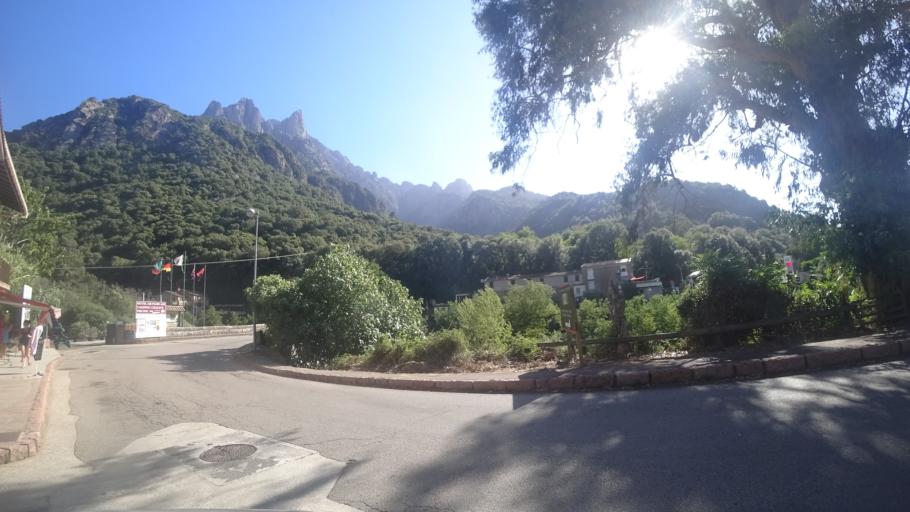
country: FR
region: Corsica
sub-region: Departement de la Corse-du-Sud
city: Cargese
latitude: 42.2625
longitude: 8.7100
